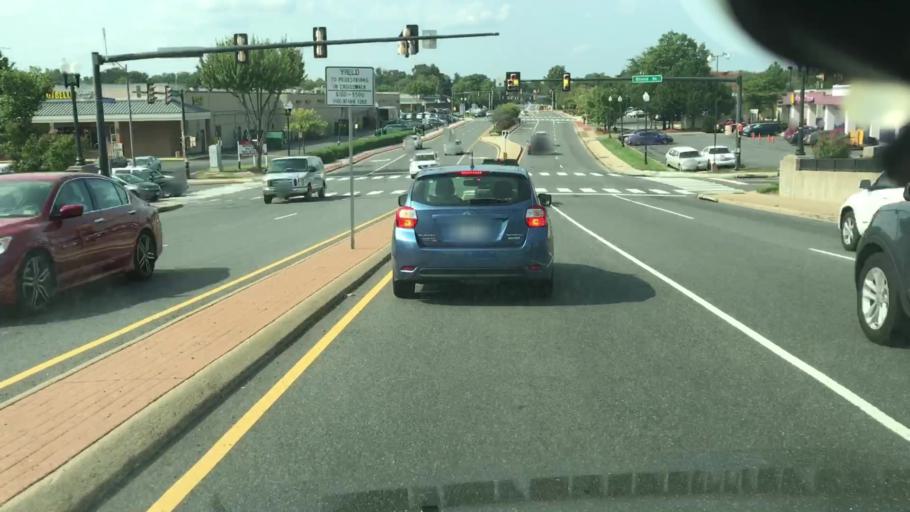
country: US
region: Virginia
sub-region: Fairfax County
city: Springfield
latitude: 38.7803
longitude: -77.1861
